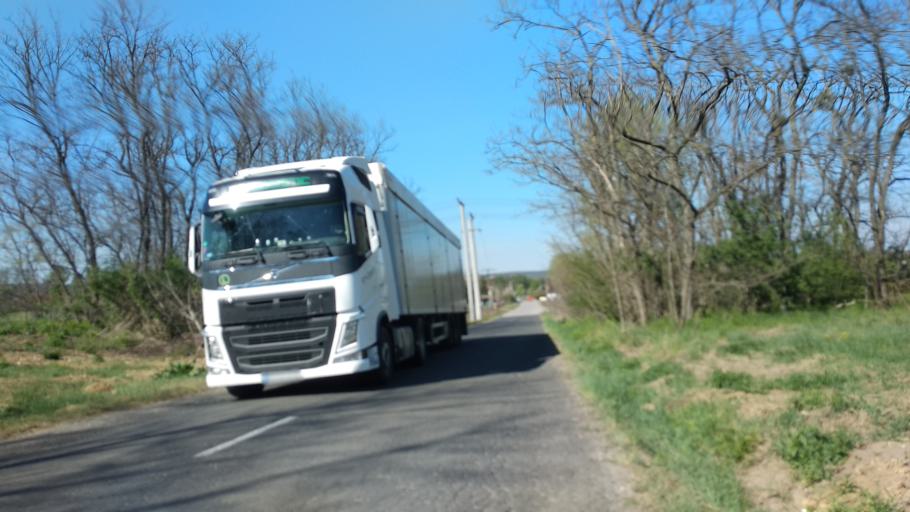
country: HU
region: Pest
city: Godollo
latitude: 47.5848
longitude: 19.3423
